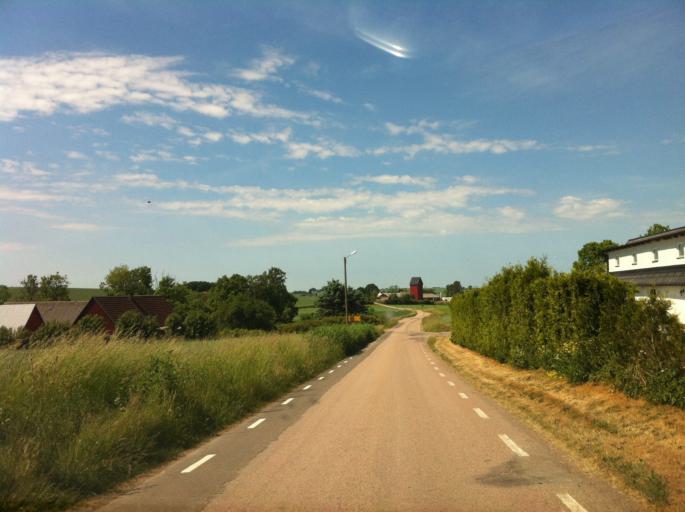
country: SE
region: Skane
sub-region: Landskrona
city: Asmundtorp
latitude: 55.9400
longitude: 12.9109
